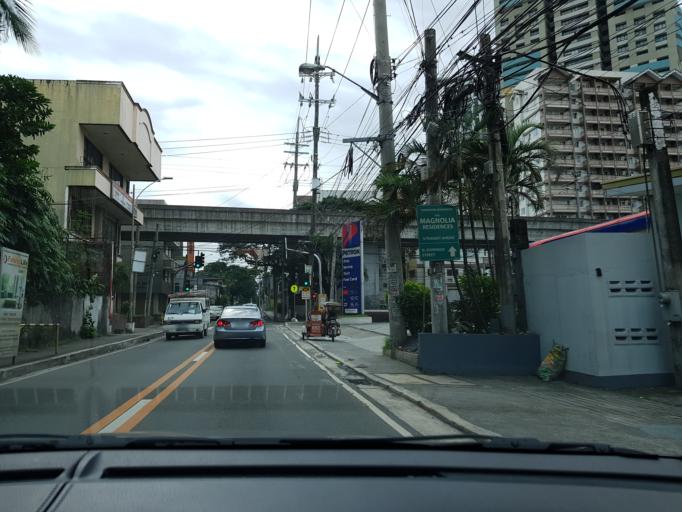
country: PH
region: Metro Manila
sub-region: San Juan
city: San Juan
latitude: 14.6172
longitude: 121.0394
